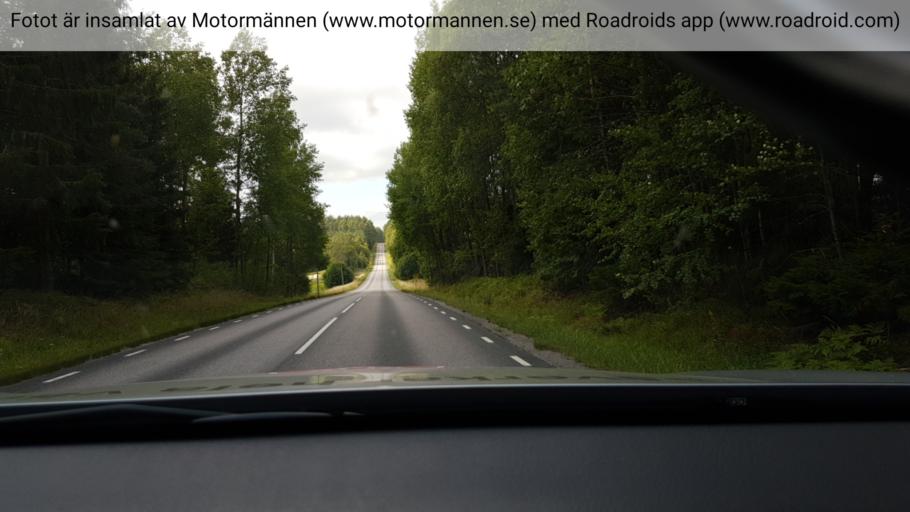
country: SE
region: Stockholm
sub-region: Norrtalje Kommun
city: Rimbo
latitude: 59.7099
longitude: 18.4246
